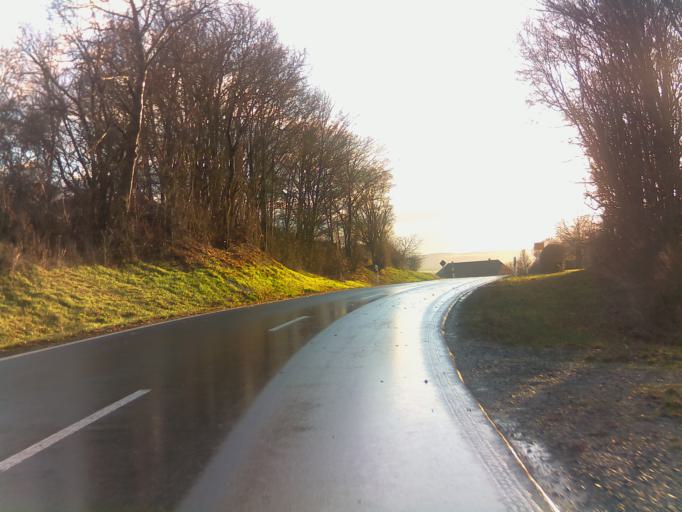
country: DE
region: Bavaria
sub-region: Regierungsbezirk Unterfranken
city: Hausen
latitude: 50.4910
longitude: 10.1361
